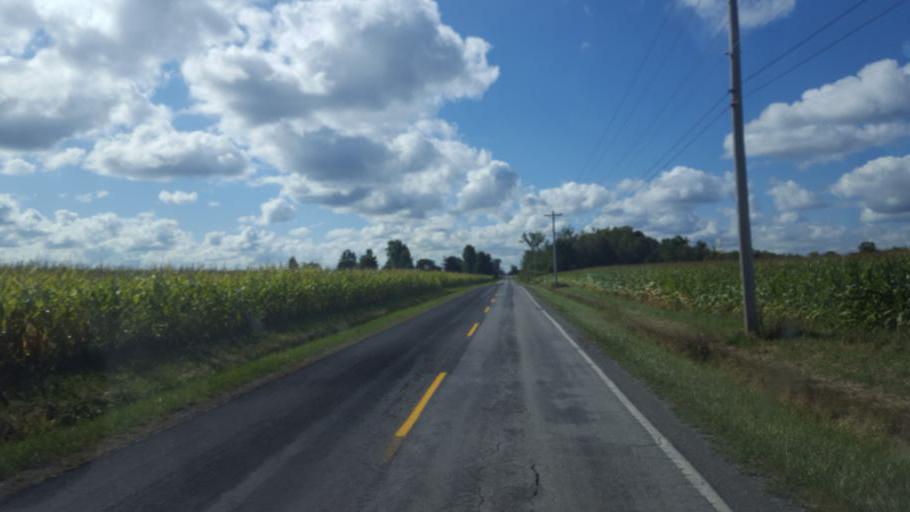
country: US
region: Ohio
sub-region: Lorain County
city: Oberlin
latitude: 41.2553
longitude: -82.1798
